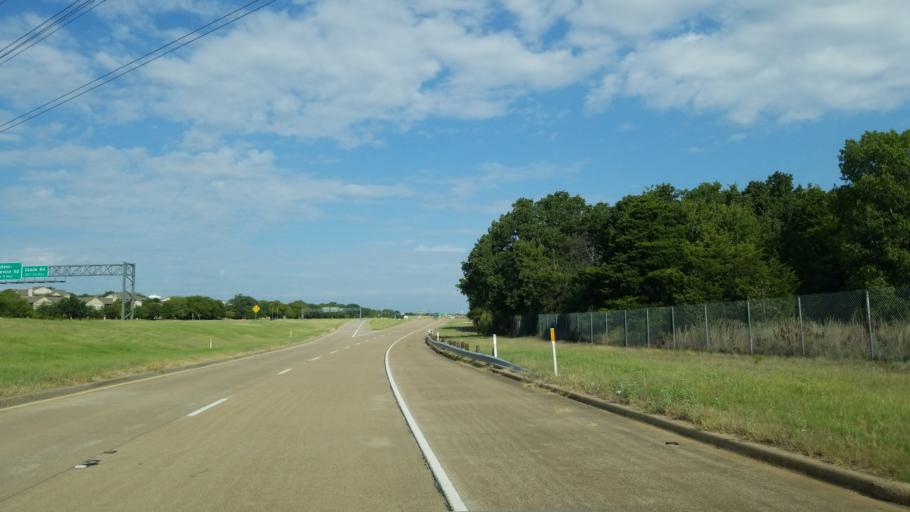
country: US
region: Texas
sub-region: Tarrant County
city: Euless
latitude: 32.8699
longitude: -97.0658
